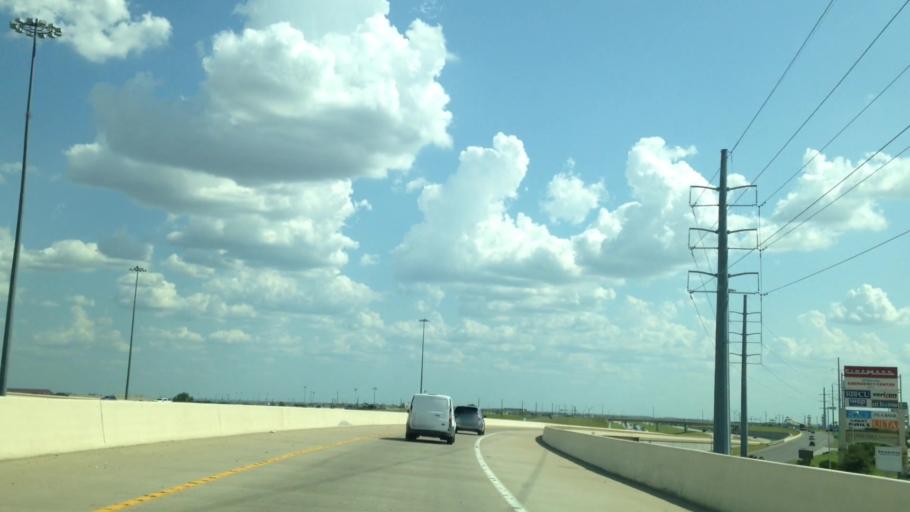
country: US
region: Texas
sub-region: Travis County
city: Pflugerville
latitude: 30.4724
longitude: -97.5940
